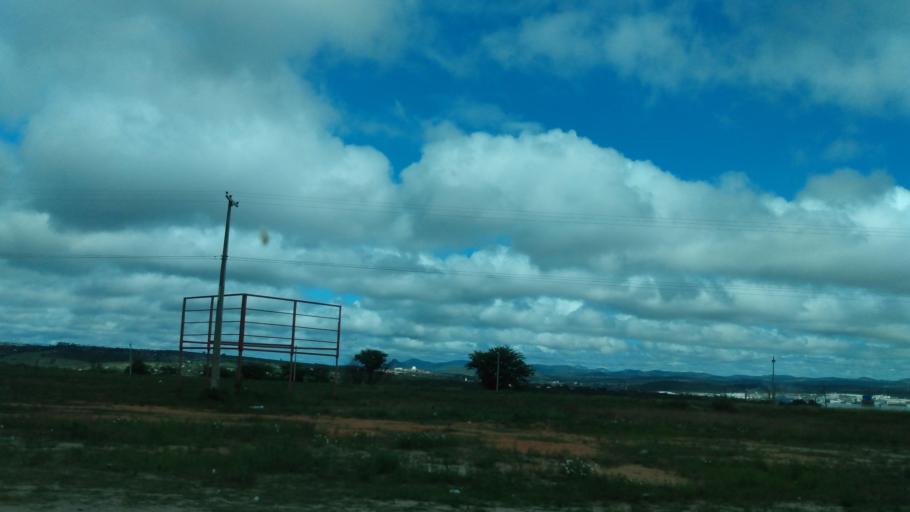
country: BR
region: Pernambuco
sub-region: Caruaru
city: Caruaru
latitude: -8.3131
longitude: -35.9911
